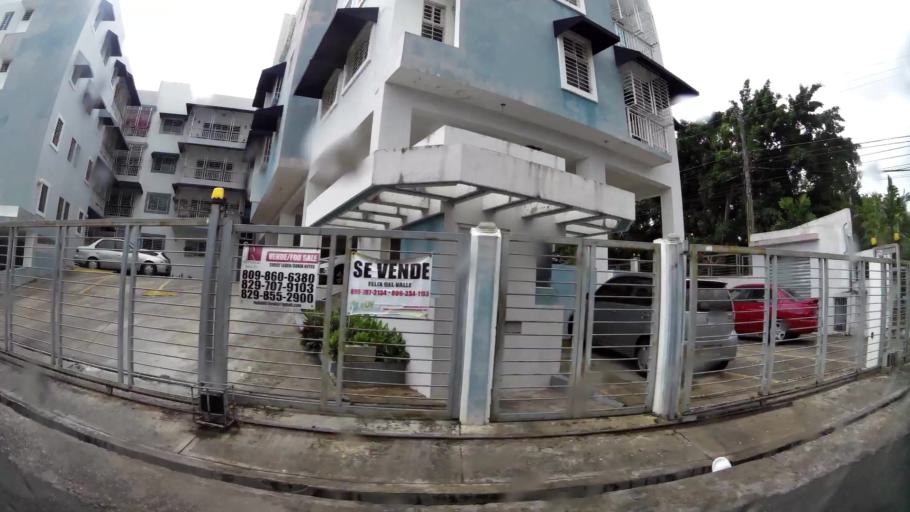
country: DO
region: Nacional
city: La Agustina
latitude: 18.5005
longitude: -69.9360
